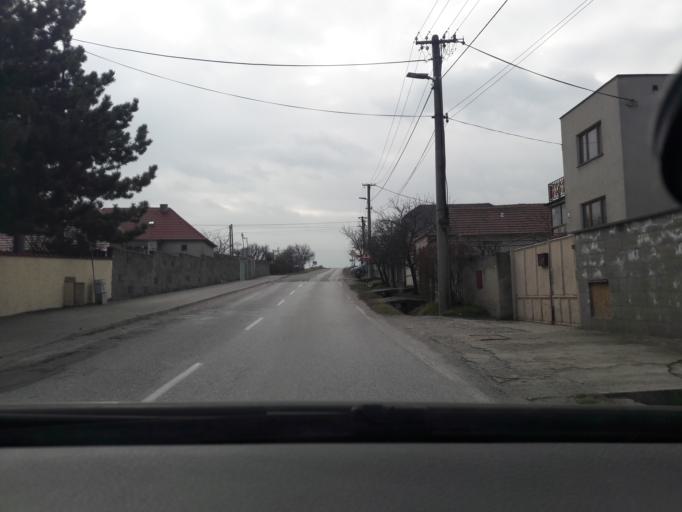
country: SK
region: Trnavsky
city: Smolenice
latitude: 48.4371
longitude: 17.4261
